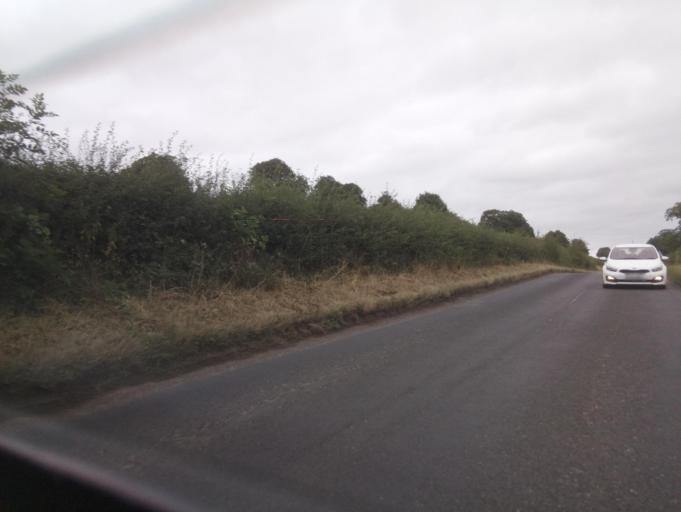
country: GB
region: England
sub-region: Derbyshire
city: Repton
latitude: 52.8176
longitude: -1.5406
